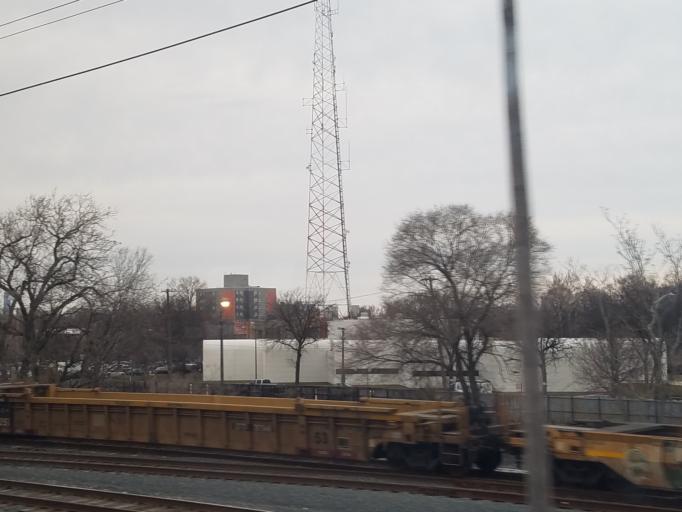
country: US
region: Illinois
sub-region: Cook County
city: Chicago
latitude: 41.7673
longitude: -87.6066
